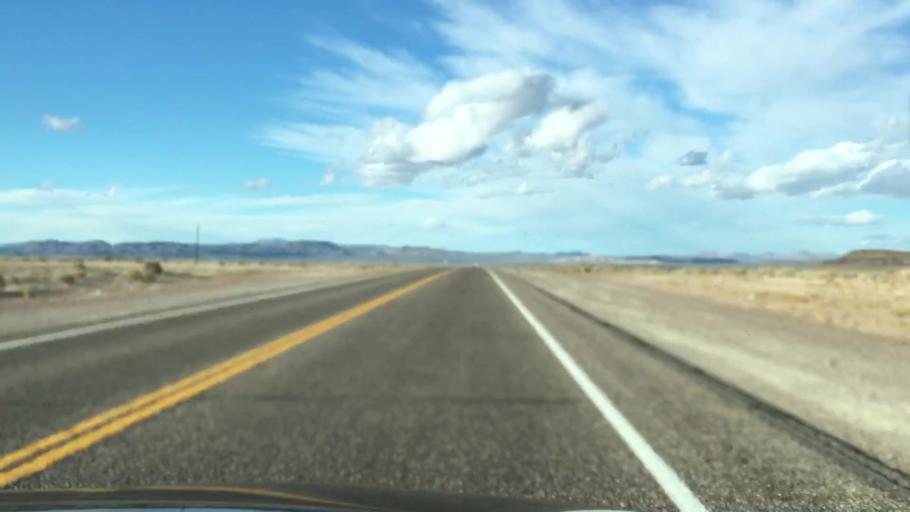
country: US
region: Nevada
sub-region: Esmeralda County
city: Goldfield
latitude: 37.3897
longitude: -117.1444
